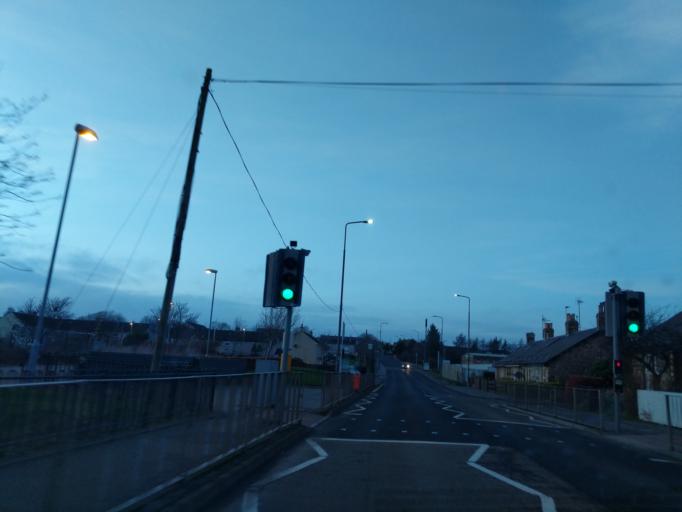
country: GB
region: Scotland
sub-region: Midlothian
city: Bonnyrigg
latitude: 55.8715
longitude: -3.0973
